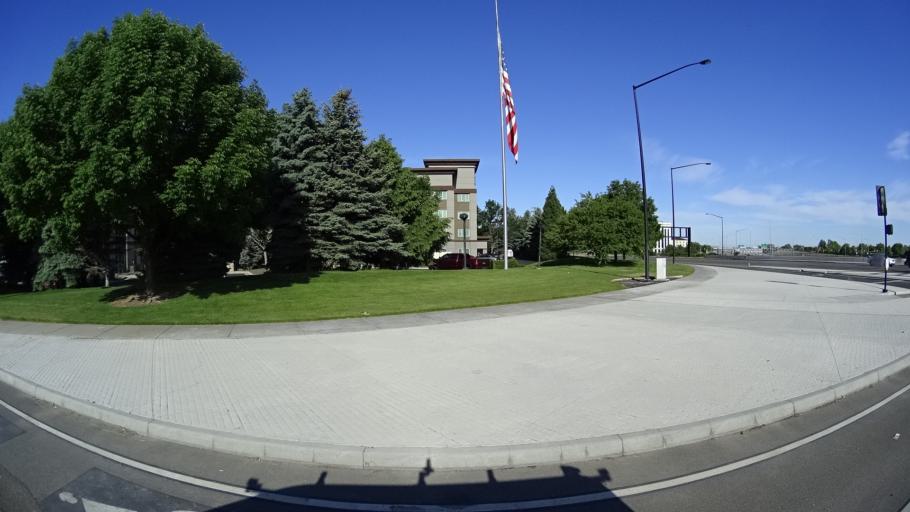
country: US
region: Idaho
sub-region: Ada County
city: Garden City
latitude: 43.5896
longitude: -116.2742
